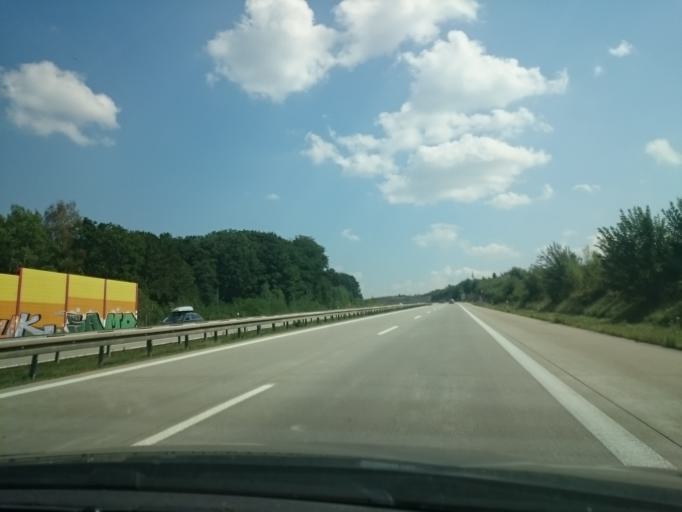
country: DE
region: Saxony
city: Hartenstein
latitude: 50.6903
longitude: 12.6756
